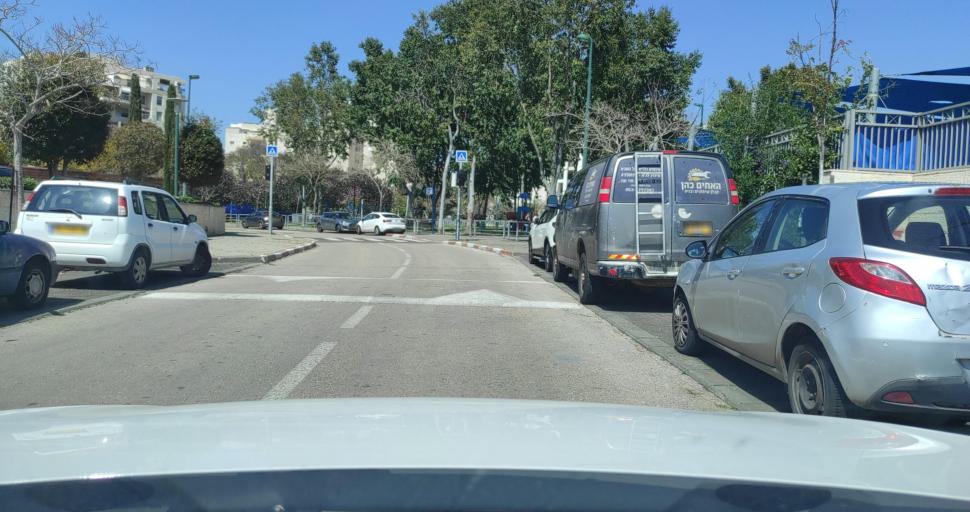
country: IL
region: Central District
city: Even Yehuda
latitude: 32.2955
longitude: 34.8714
